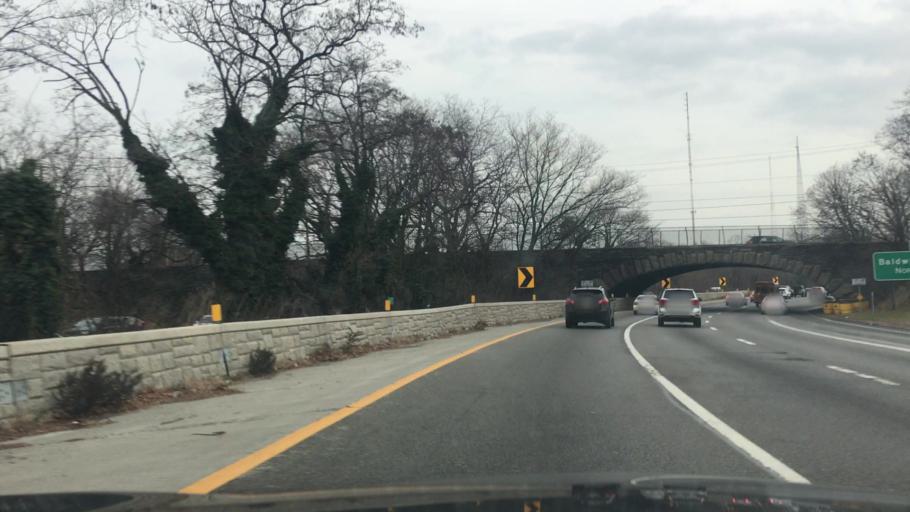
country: US
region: New York
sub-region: Nassau County
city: South Hempstead
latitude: 40.6872
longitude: -73.6155
